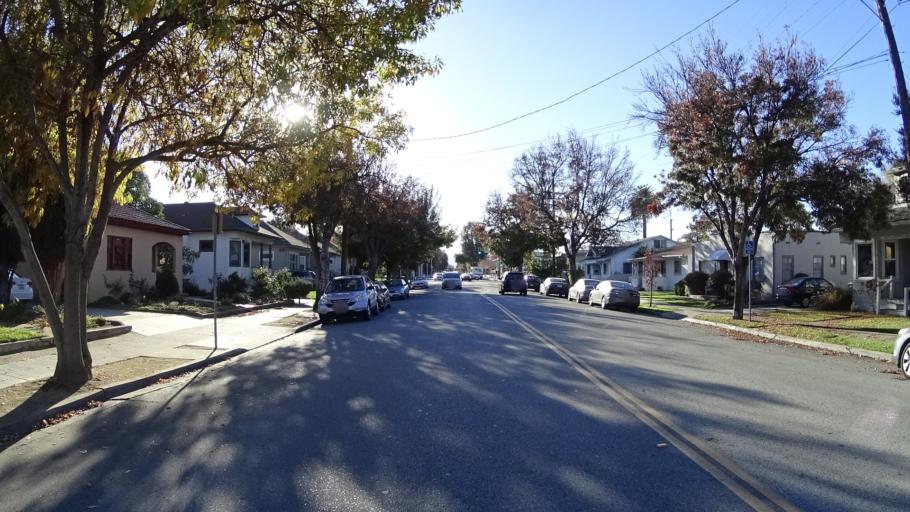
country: US
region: California
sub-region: Santa Clara County
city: Santa Clara
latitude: 37.3515
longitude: -121.9429
